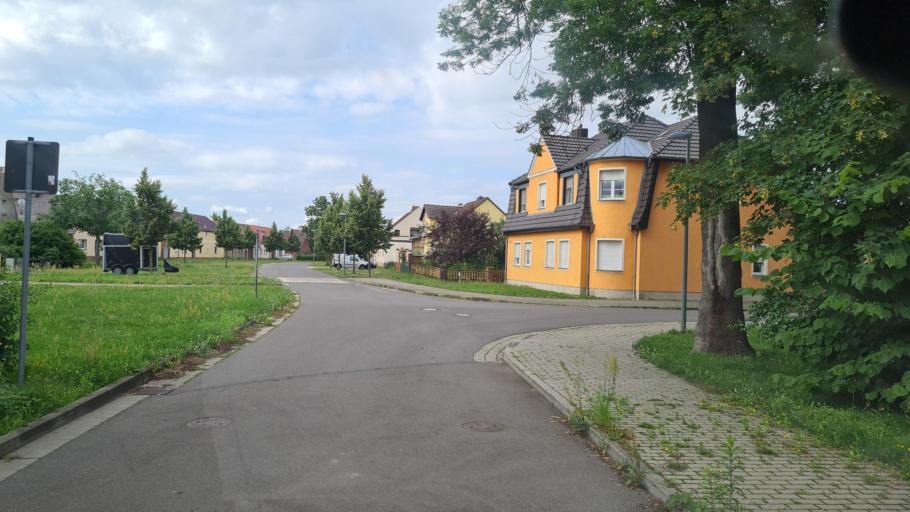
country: DE
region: Brandenburg
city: Grossraschen
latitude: 51.5515
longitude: 14.0615
